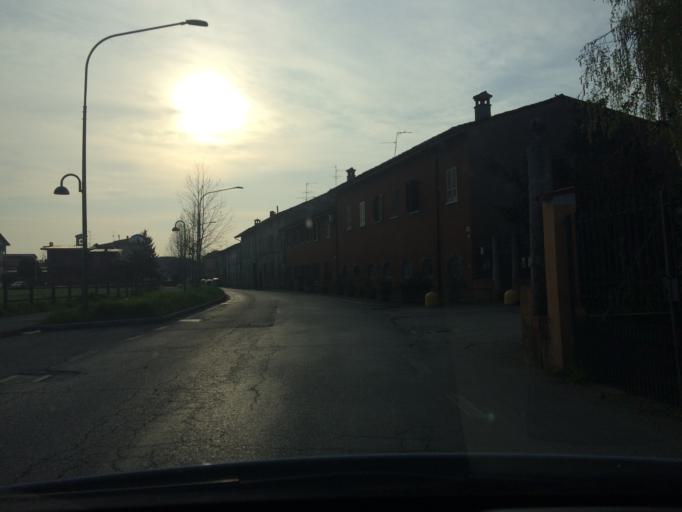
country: IT
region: Lombardy
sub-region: Provincia di Brescia
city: Flero
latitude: 45.5008
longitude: 10.1767
